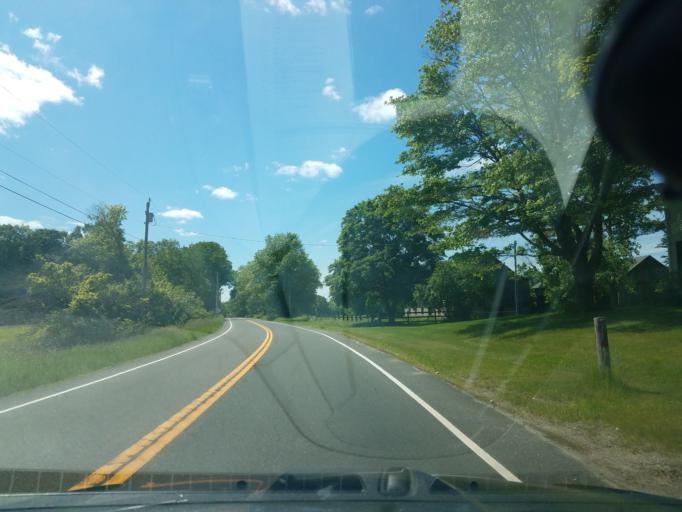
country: US
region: Massachusetts
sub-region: Berkshire County
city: New Marlborough
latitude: 42.0417
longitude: -73.2176
